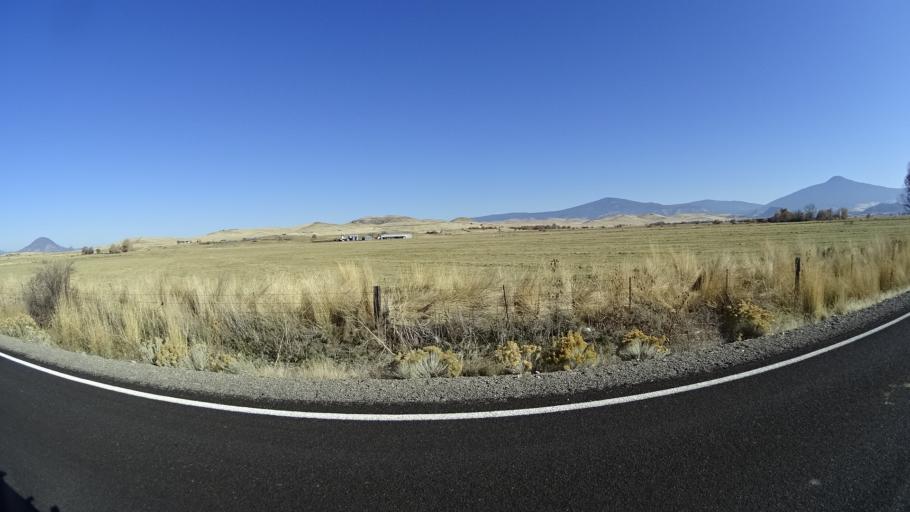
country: US
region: California
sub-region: Siskiyou County
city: Montague
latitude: 41.7159
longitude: -122.4452
